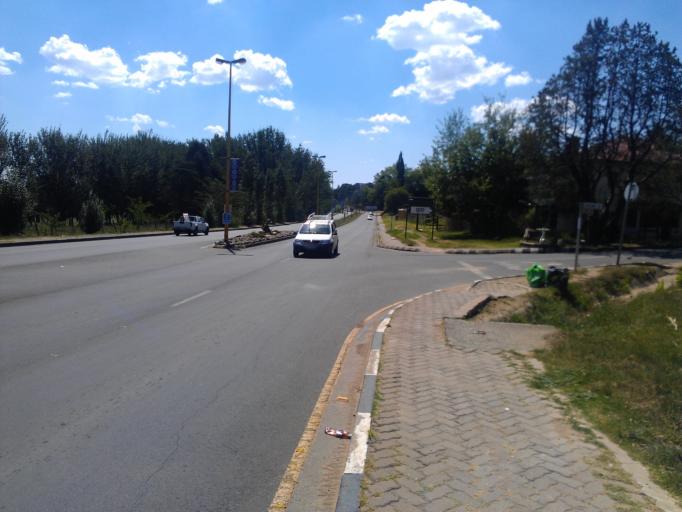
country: LS
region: Maseru
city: Maseru
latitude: -29.3102
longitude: 27.4755
